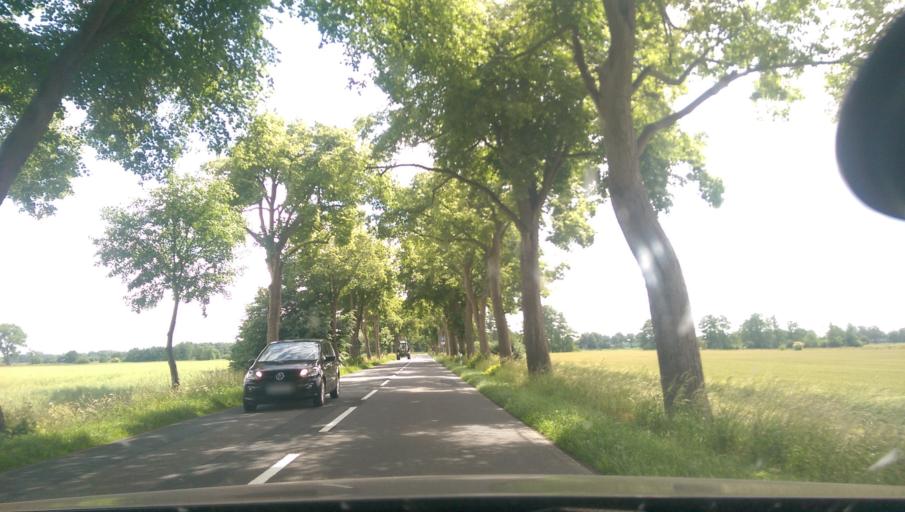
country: DE
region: Lower Saxony
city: Oyten
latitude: 53.0970
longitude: 9.0579
